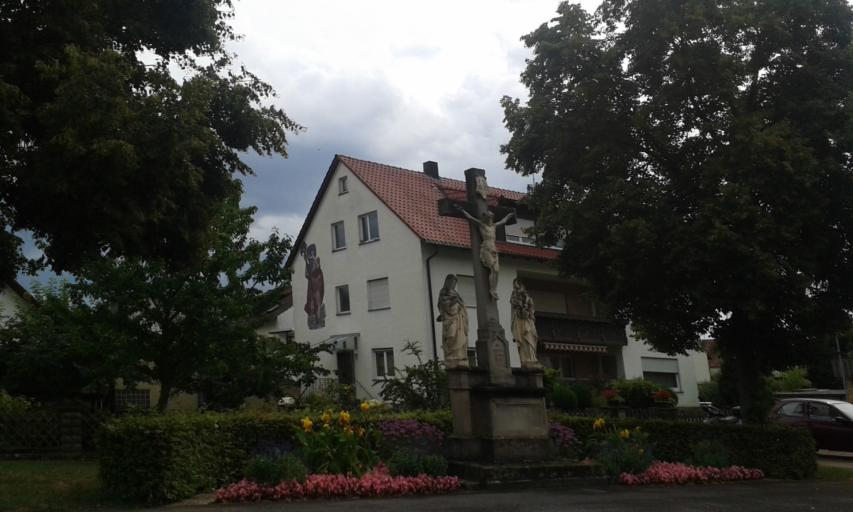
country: DE
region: Bavaria
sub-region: Upper Franconia
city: Bamberg
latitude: 49.8646
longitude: 10.9104
